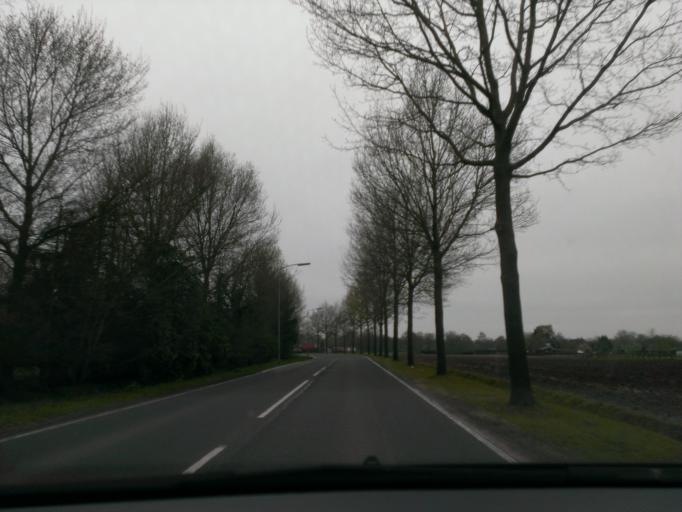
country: NL
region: Gelderland
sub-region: Gemeente Epe
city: Vaassen
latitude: 52.2926
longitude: 5.9838
